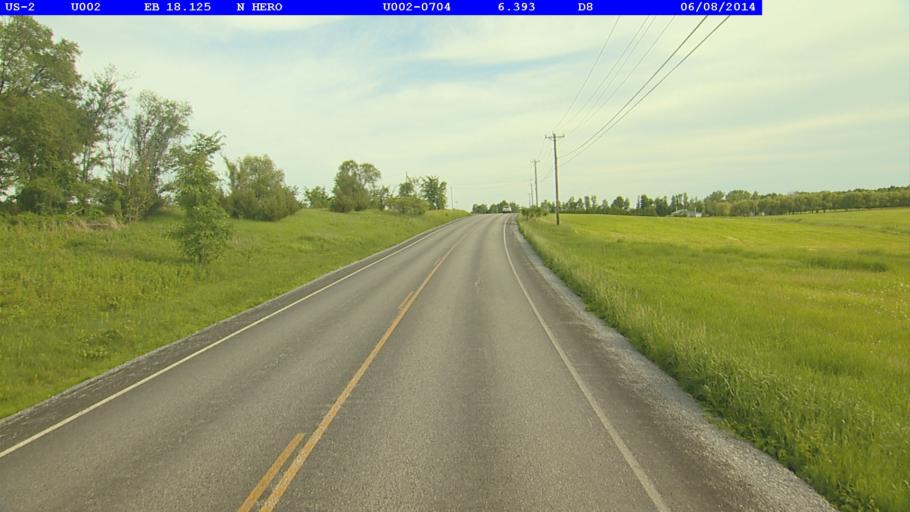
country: US
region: Vermont
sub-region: Grand Isle County
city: North Hero
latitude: 44.8073
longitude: -73.2917
